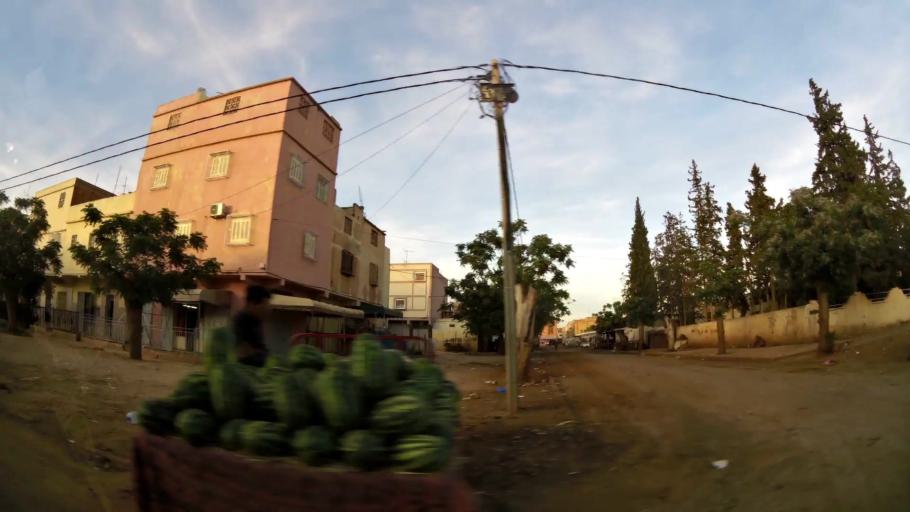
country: MA
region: Oriental
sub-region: Oujda-Angad
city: Oujda
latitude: 34.6808
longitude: -1.8841
